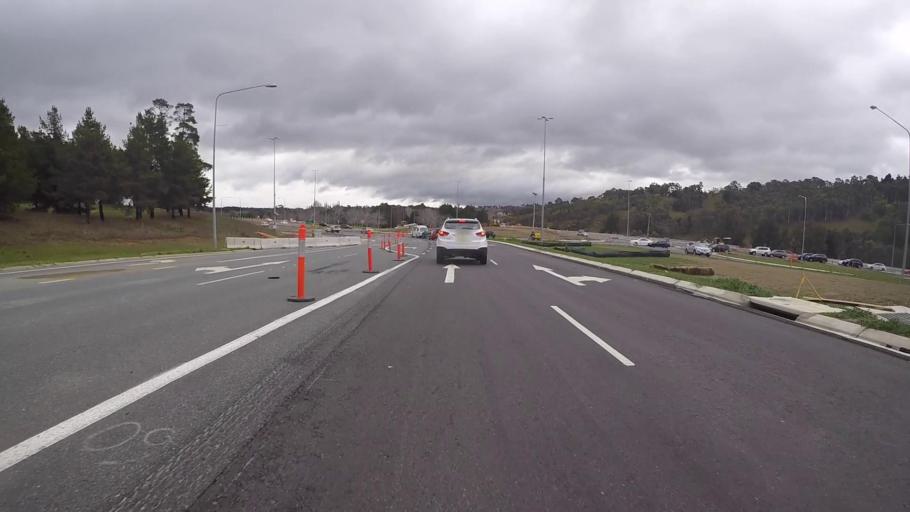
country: AU
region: Australian Capital Territory
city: Kaleen
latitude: -35.2022
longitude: 149.0954
